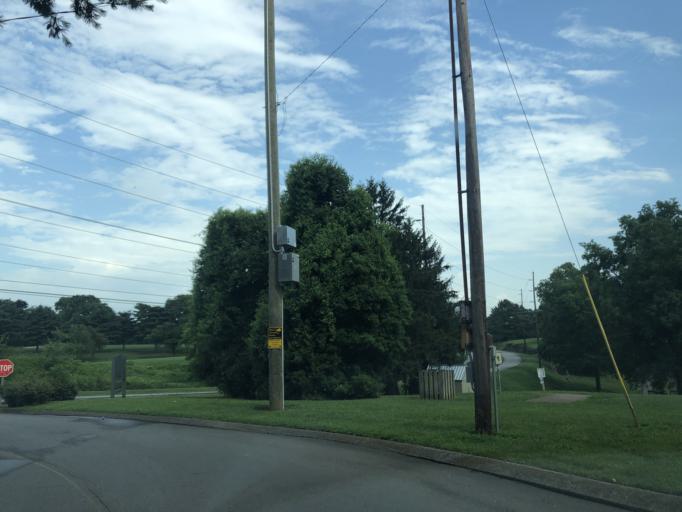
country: US
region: Tennessee
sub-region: Davidson County
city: Lakewood
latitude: 36.1864
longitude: -86.6867
